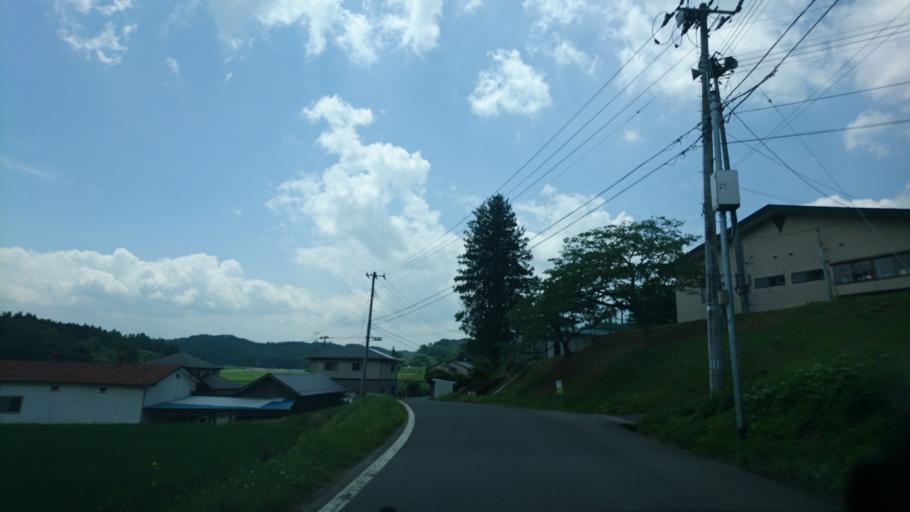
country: JP
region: Iwate
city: Ichinoseki
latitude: 38.9077
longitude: 141.2238
